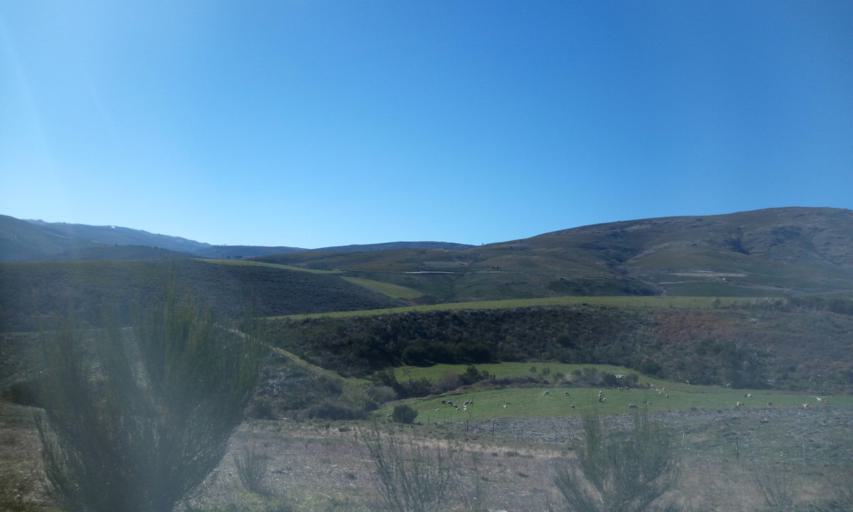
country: PT
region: Guarda
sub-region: Manteigas
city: Manteigas
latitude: 40.4609
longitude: -7.4971
